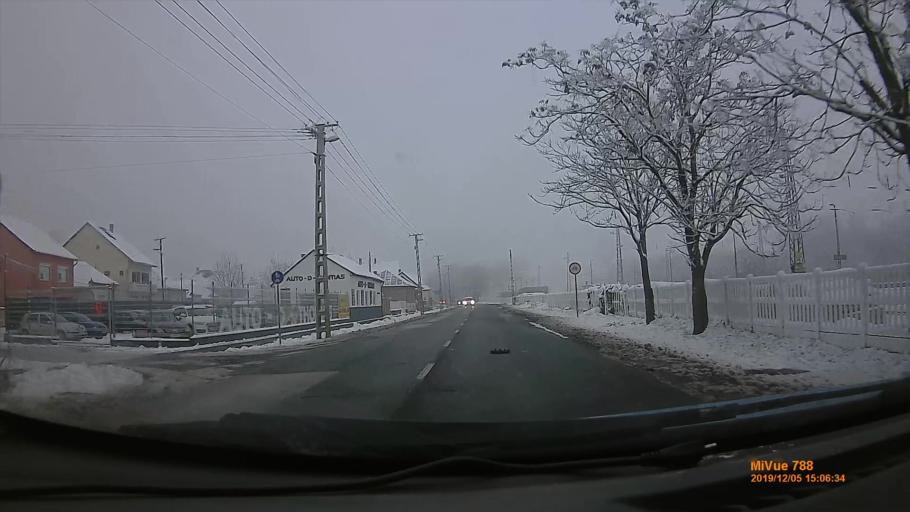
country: HU
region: Szabolcs-Szatmar-Bereg
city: Rakamaz
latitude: 48.1185
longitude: 21.4767
